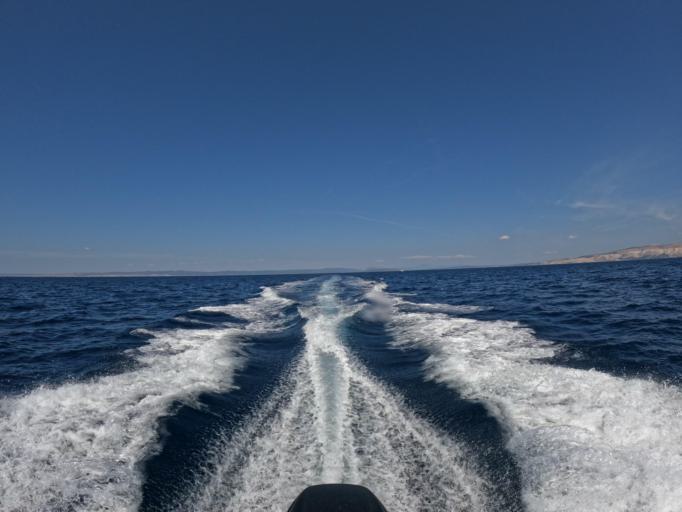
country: HR
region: Primorsko-Goranska
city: Lopar
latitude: 44.8657
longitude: 14.6795
